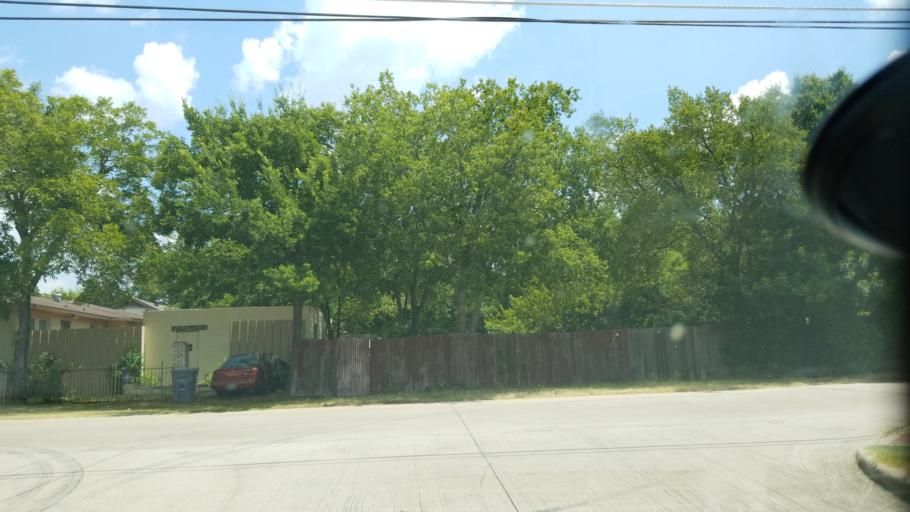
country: US
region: Texas
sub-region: Dallas County
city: Duncanville
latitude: 32.6810
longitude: -96.9042
